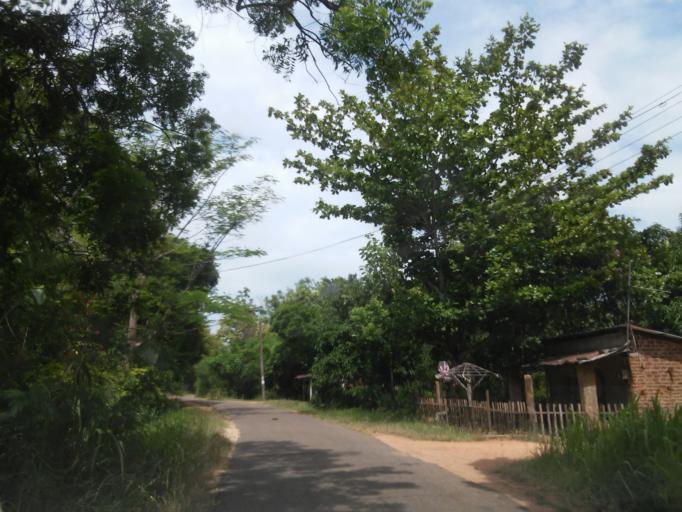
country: LK
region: Central
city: Sigiriya
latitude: 8.0875
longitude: 80.6735
